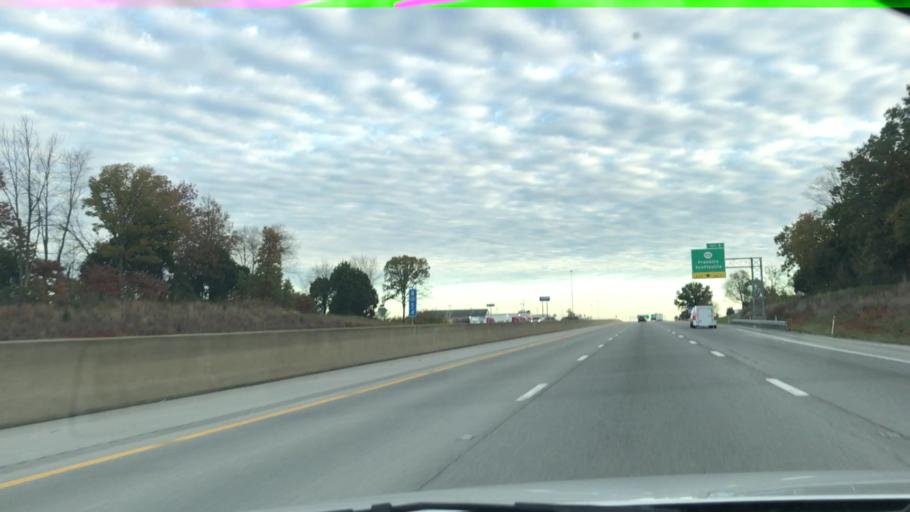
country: US
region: Kentucky
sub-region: Simpson County
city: Franklin
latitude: 36.7074
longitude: -86.5265
